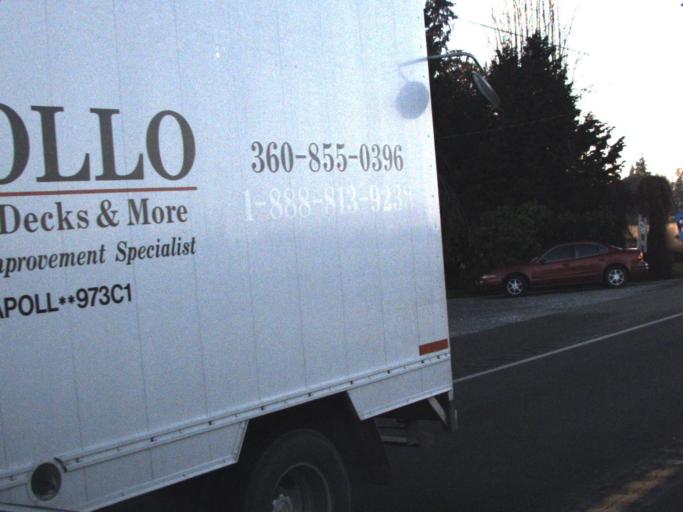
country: US
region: Washington
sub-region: Skagit County
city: Mount Vernon
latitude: 48.4344
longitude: -122.3748
